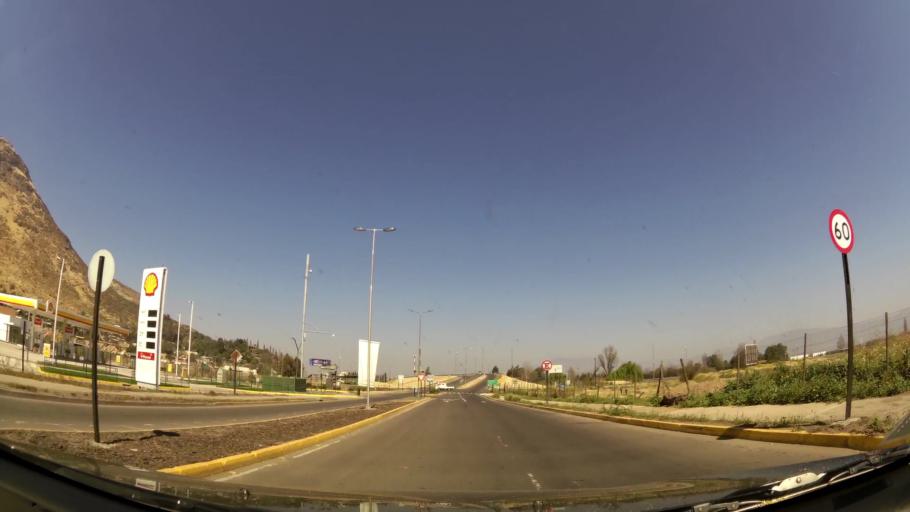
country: CL
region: Santiago Metropolitan
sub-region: Provincia de Chacabuco
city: Chicureo Abajo
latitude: -33.3032
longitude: -70.6971
